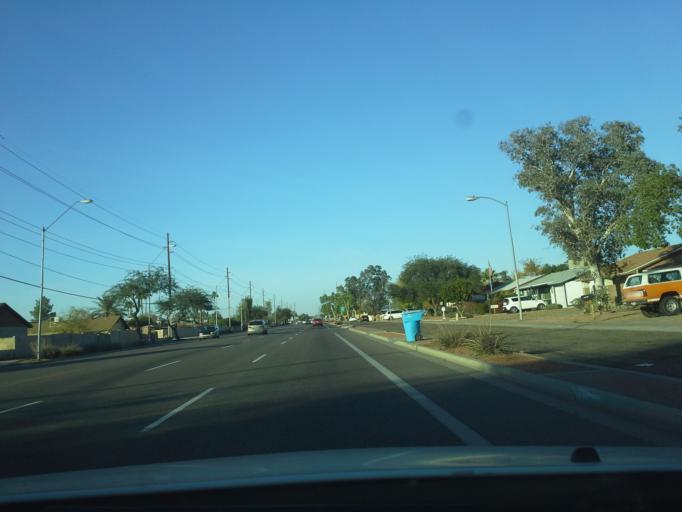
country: US
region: Arizona
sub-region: Maricopa County
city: Glendale
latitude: 33.6485
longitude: -112.1344
